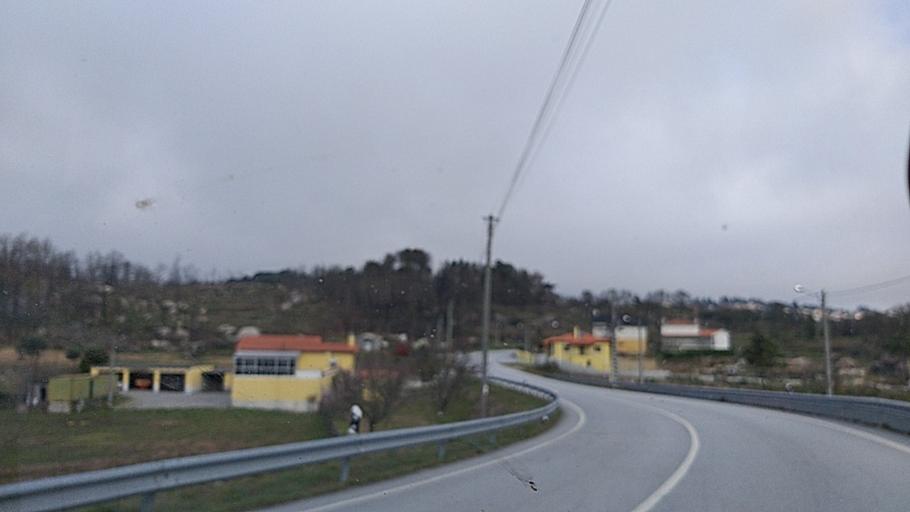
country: PT
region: Guarda
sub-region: Fornos de Algodres
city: Fornos de Algodres
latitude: 40.6765
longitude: -7.4718
